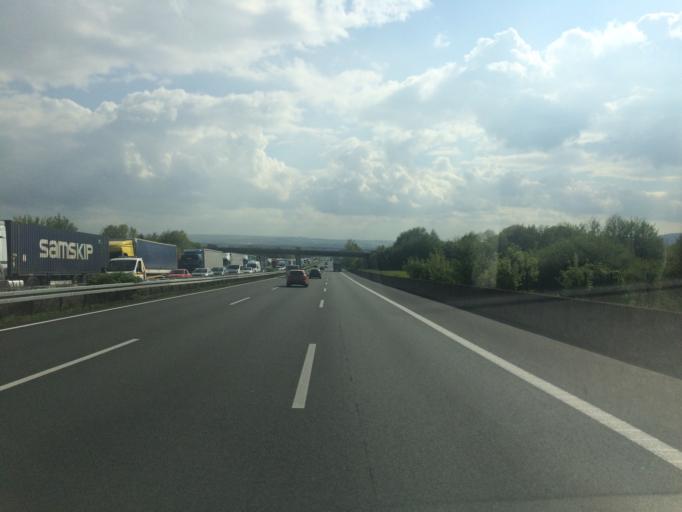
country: DE
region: Lower Saxony
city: Rodenberg
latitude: 52.3147
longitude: 9.3815
